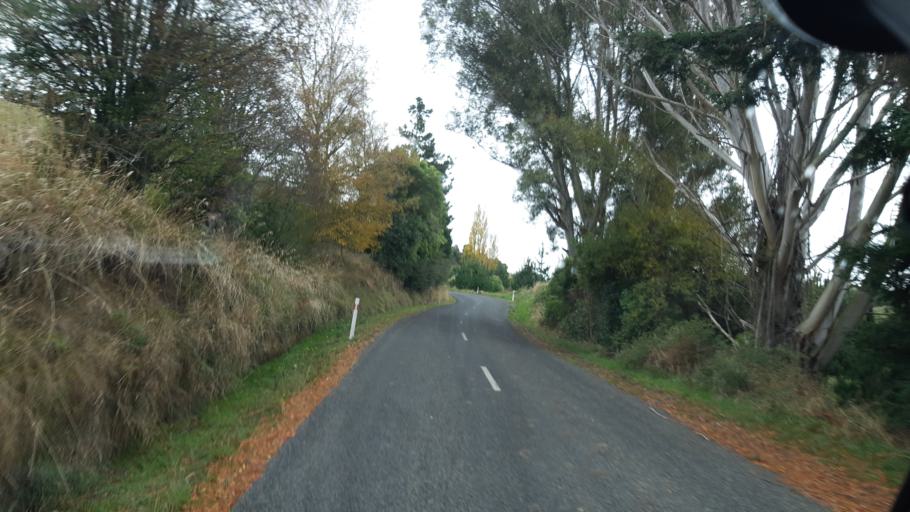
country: NZ
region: Manawatu-Wanganui
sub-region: Ruapehu District
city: Waiouru
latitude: -39.5546
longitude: 175.6151
